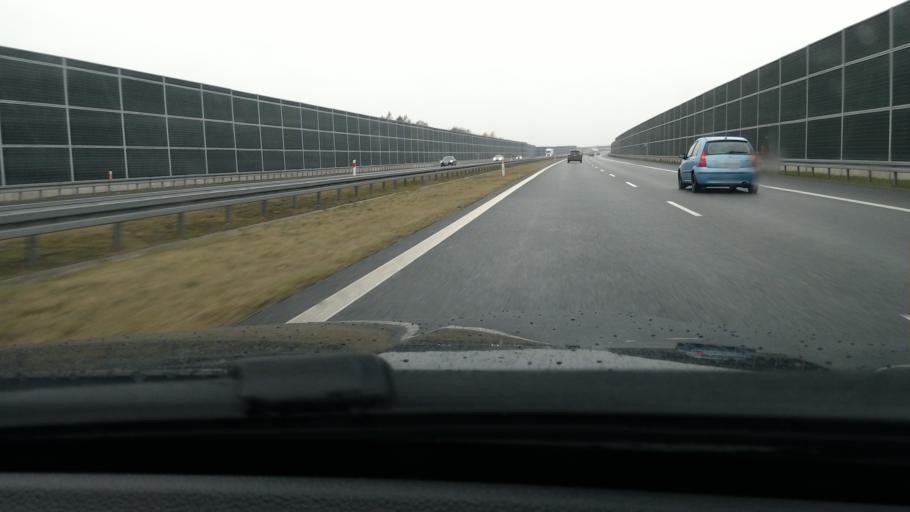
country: PL
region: Masovian Voivodeship
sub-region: Powiat zyrardowski
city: Guzow
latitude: 52.0731
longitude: 20.3017
